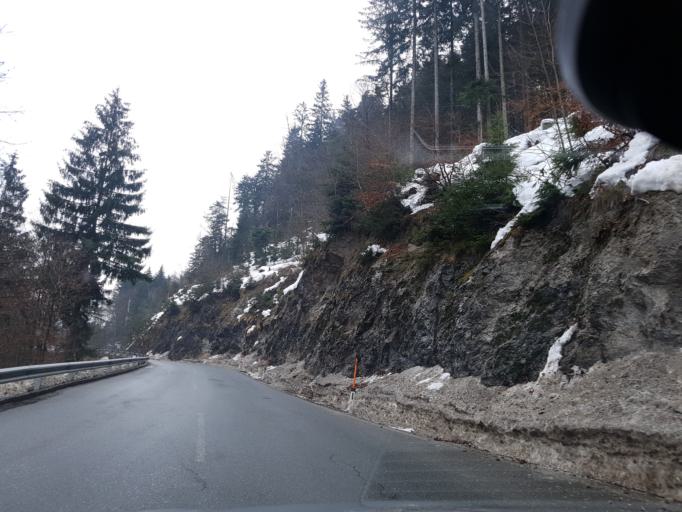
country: AT
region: Tyrol
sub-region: Politischer Bezirk Kufstein
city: Worgl
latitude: 47.4731
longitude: 12.0736
